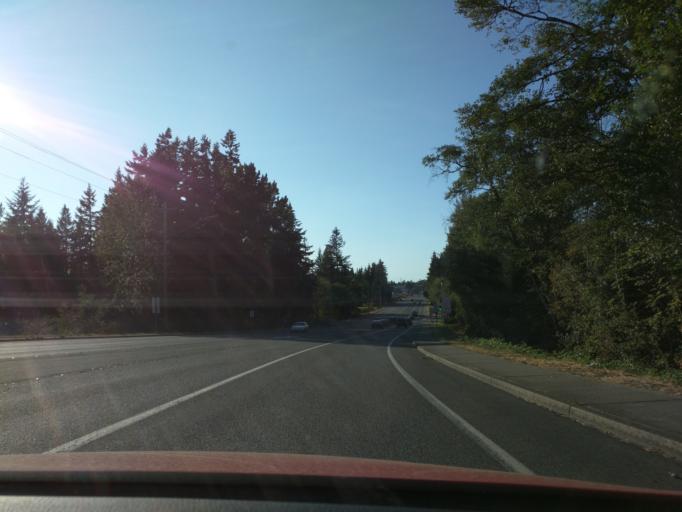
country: US
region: Washington
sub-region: Snohomish County
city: Martha Lake
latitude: 47.8830
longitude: -122.2529
